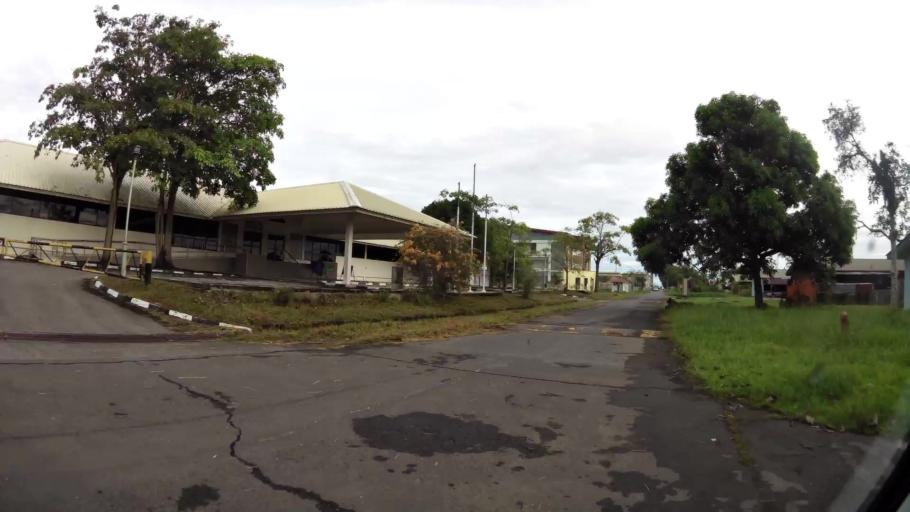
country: BN
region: Belait
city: Seria
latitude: 4.6067
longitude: 114.3327
